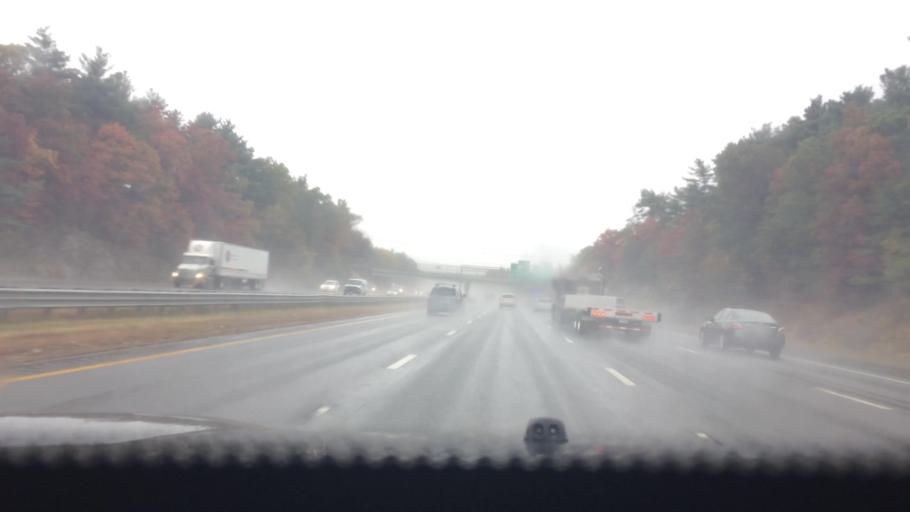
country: US
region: Massachusetts
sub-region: Middlesex County
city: Wilmington
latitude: 42.5673
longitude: -71.1456
